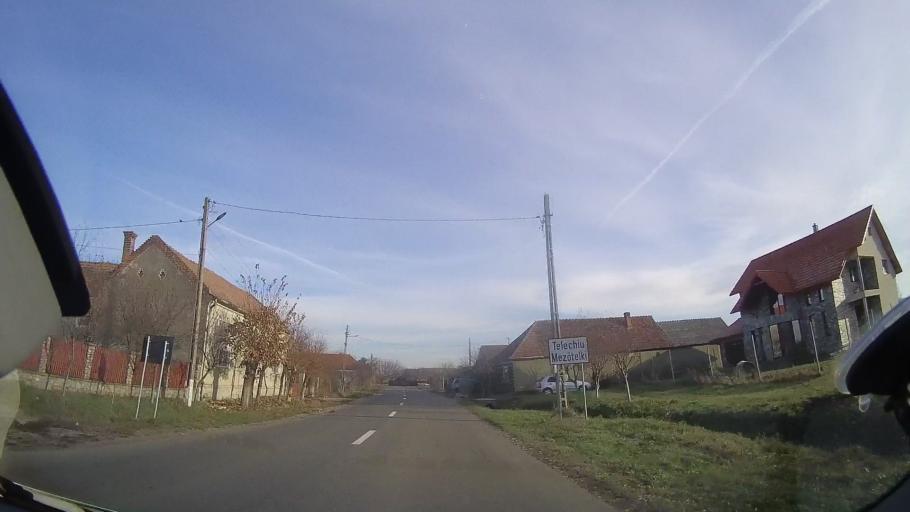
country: RO
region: Bihor
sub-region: Comuna Tetchea
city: Hotar
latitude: 47.0553
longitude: 22.2664
